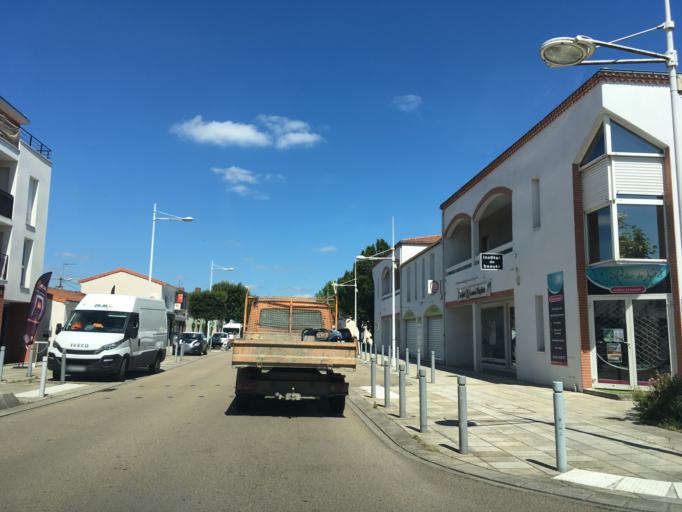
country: FR
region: Pays de la Loire
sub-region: Departement de la Loire-Atlantique
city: Les Sorinieres
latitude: 47.1475
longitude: -1.5301
